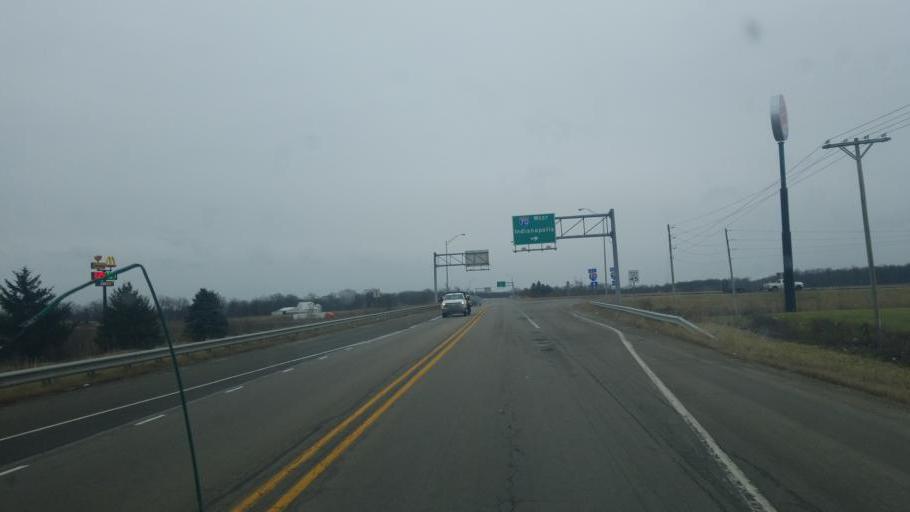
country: US
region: Indiana
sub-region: Henry County
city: Knightstown
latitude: 39.8423
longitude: -85.5575
